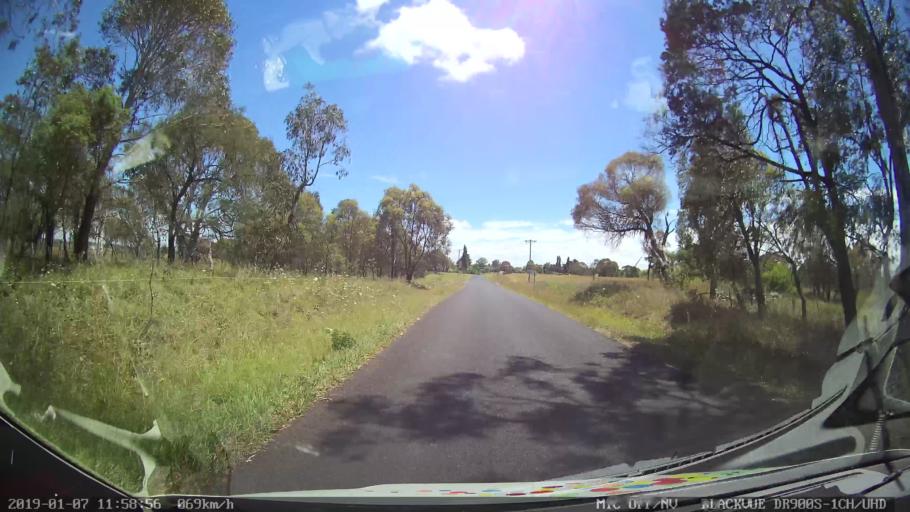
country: AU
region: New South Wales
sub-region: Guyra
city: Guyra
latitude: -30.2479
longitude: 151.6688
